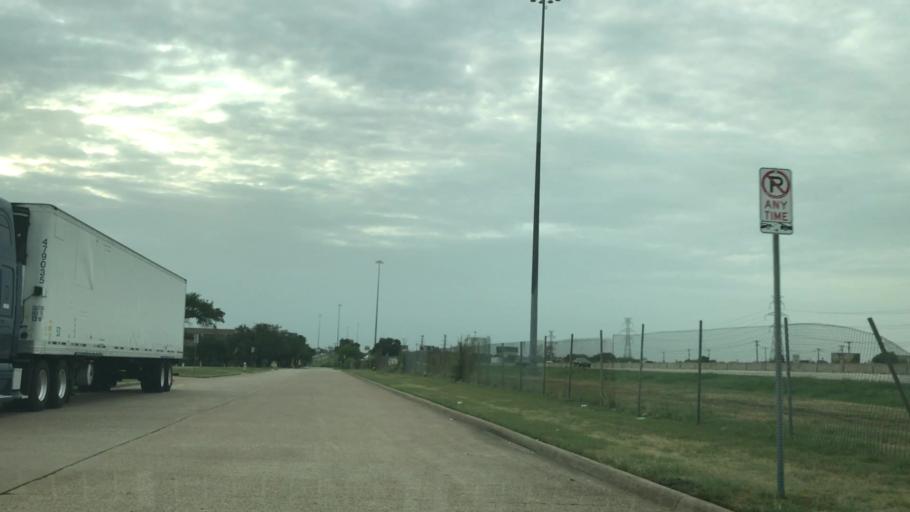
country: US
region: Texas
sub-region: Dallas County
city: Garland
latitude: 32.8805
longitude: -96.6921
